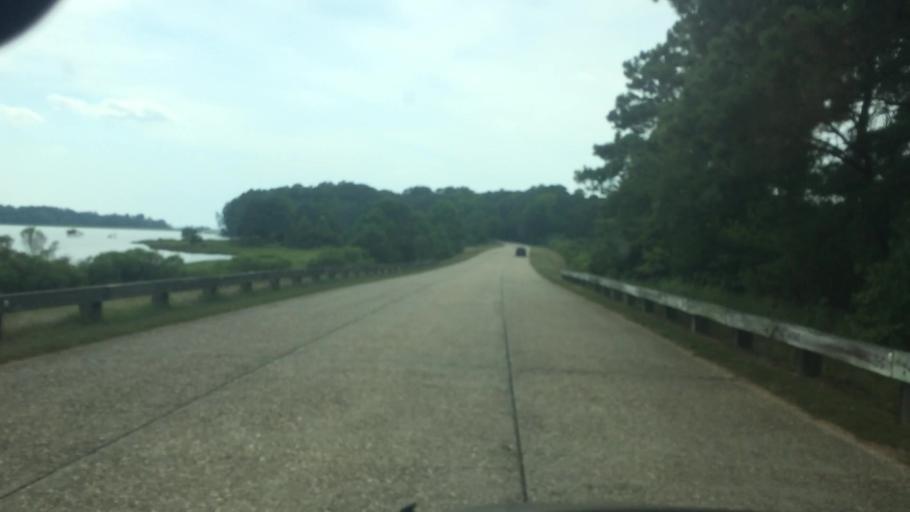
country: US
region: Virginia
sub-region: James City County
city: Williamsburg
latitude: 37.2150
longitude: -76.7443
